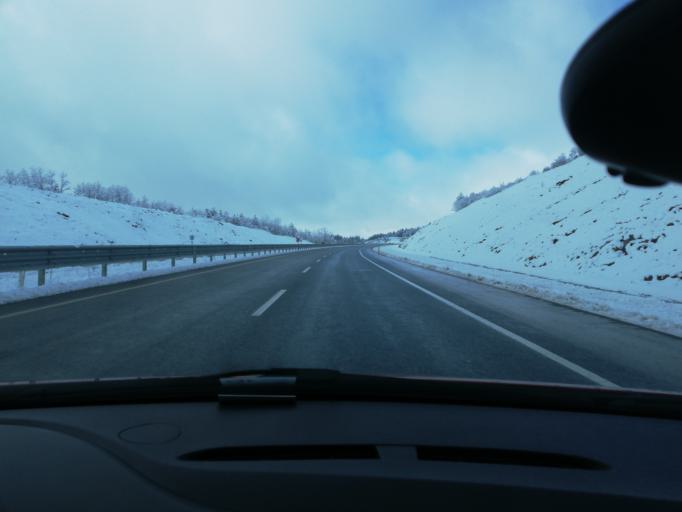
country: TR
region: Kastamonu
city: Ihsangazi
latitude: 41.3255
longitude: 33.6133
